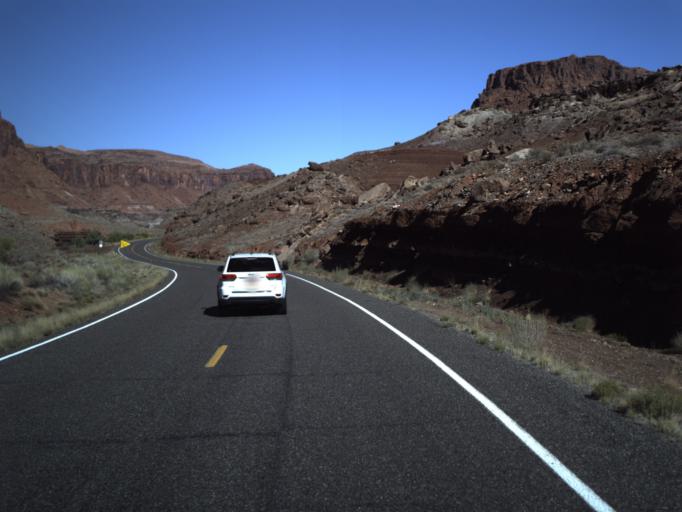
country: US
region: Utah
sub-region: San Juan County
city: Blanding
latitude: 37.8969
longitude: -110.4467
